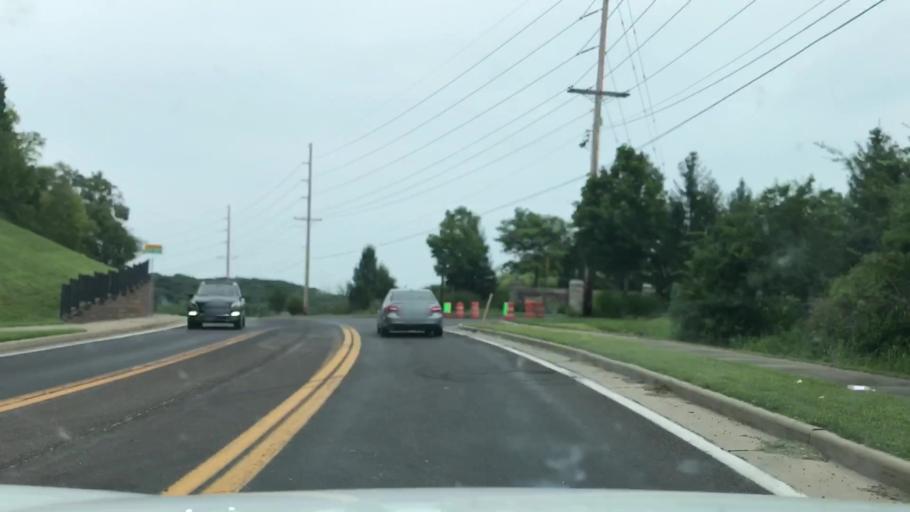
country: US
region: Missouri
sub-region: Saint Louis County
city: Clarkson Valley
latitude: 38.6475
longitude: -90.6157
